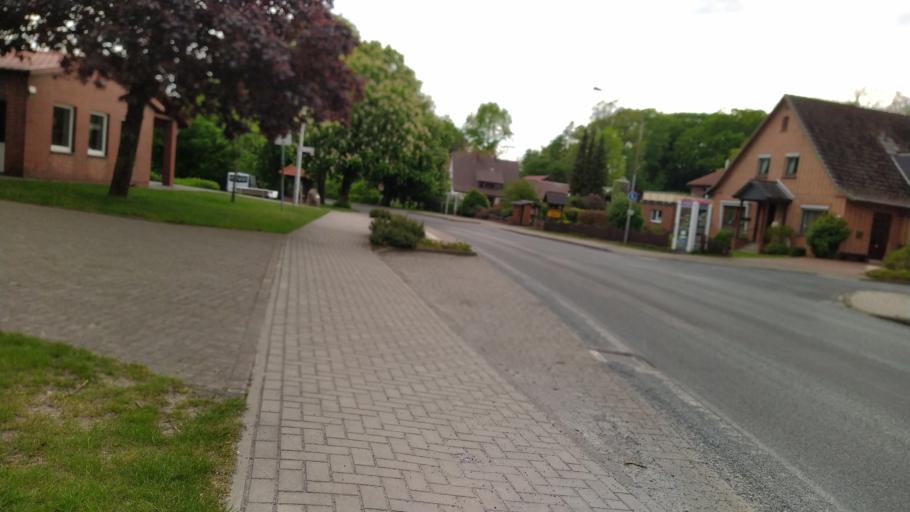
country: DE
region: Lower Saxony
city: Kirchtimke
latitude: 53.2532
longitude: 9.1528
